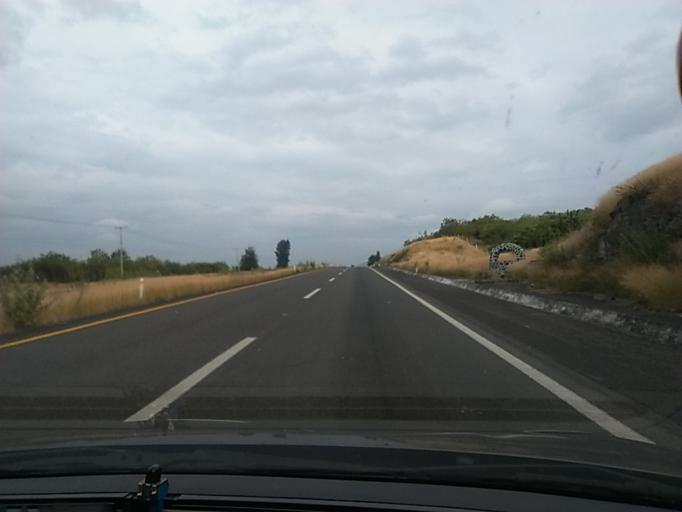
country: MX
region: Michoacan
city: Ecuandureo
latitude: 20.1714
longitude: -102.1527
